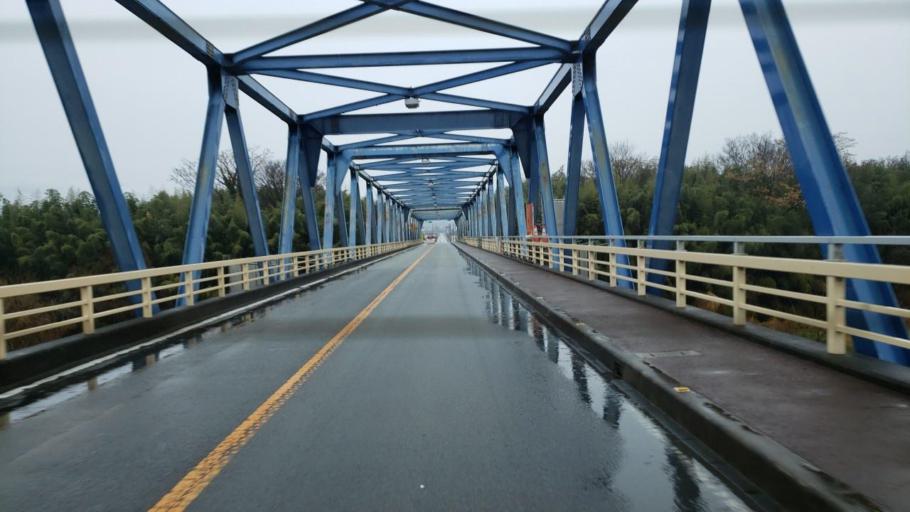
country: JP
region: Tokushima
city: Kamojimacho-jogejima
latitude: 34.0726
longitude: 134.2811
